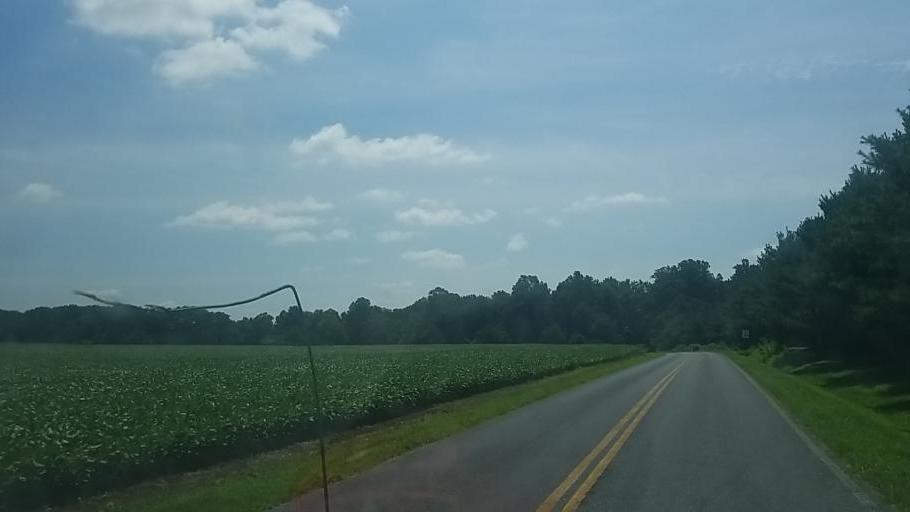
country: US
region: Maryland
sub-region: Caroline County
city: Ridgely
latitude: 38.9125
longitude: -75.9372
